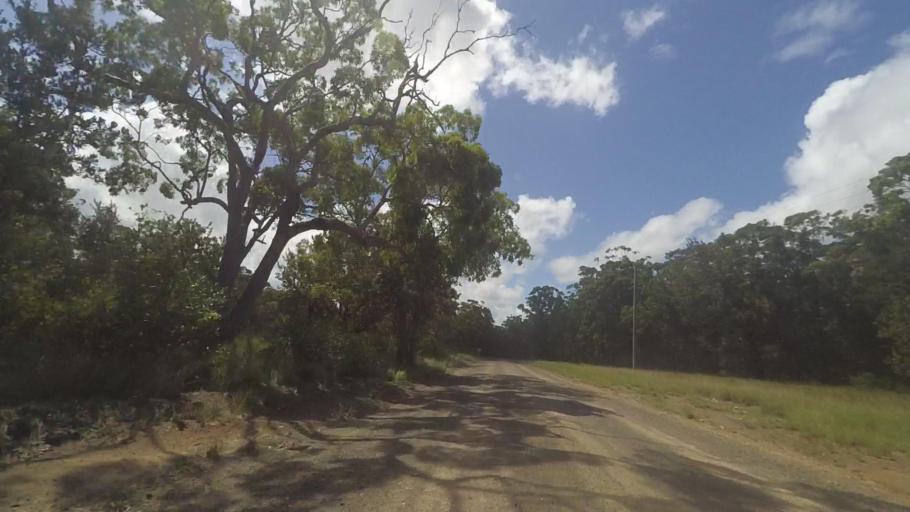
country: AU
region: New South Wales
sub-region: Great Lakes
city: Bulahdelah
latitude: -32.5048
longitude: 152.2911
